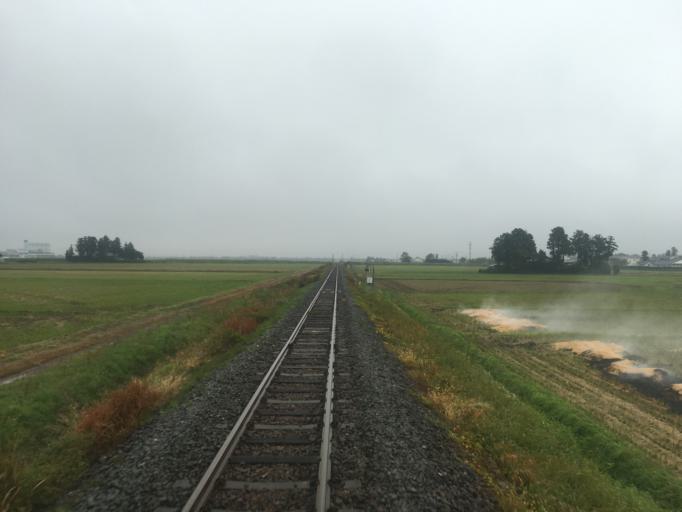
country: JP
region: Miyagi
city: Furukawa
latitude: 38.5745
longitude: 140.9042
